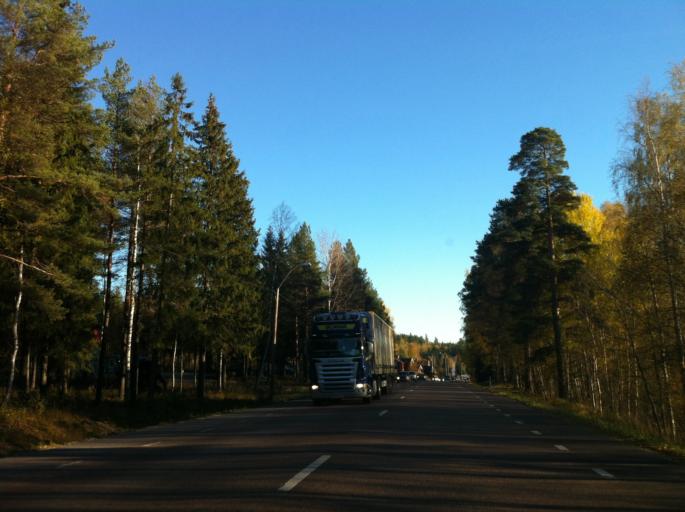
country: SE
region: Dalarna
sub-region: Faluns Kommun
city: Grycksbo
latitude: 60.6850
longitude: 15.4989
